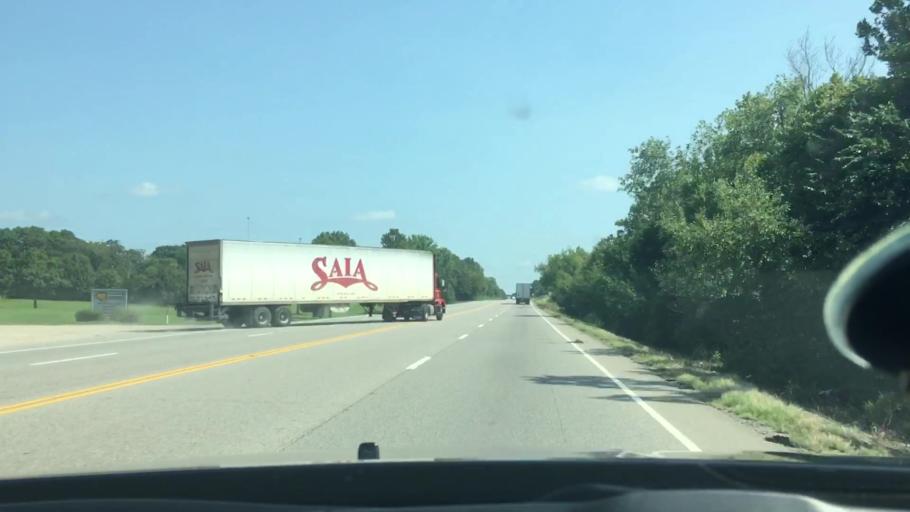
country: US
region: Oklahoma
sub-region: Atoka County
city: Atoka
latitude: 34.3345
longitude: -96.1584
